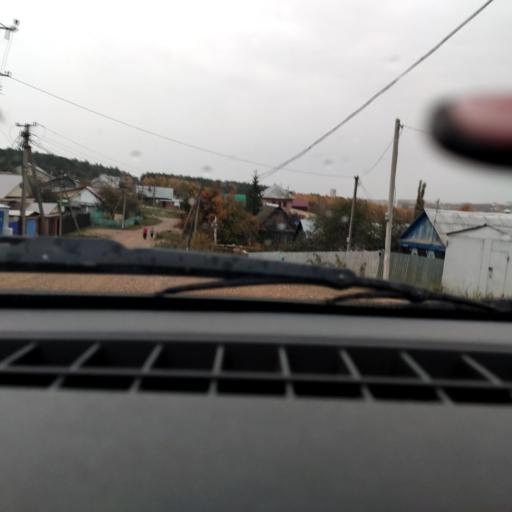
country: RU
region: Bashkortostan
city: Ufa
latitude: 54.8330
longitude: 56.1449
